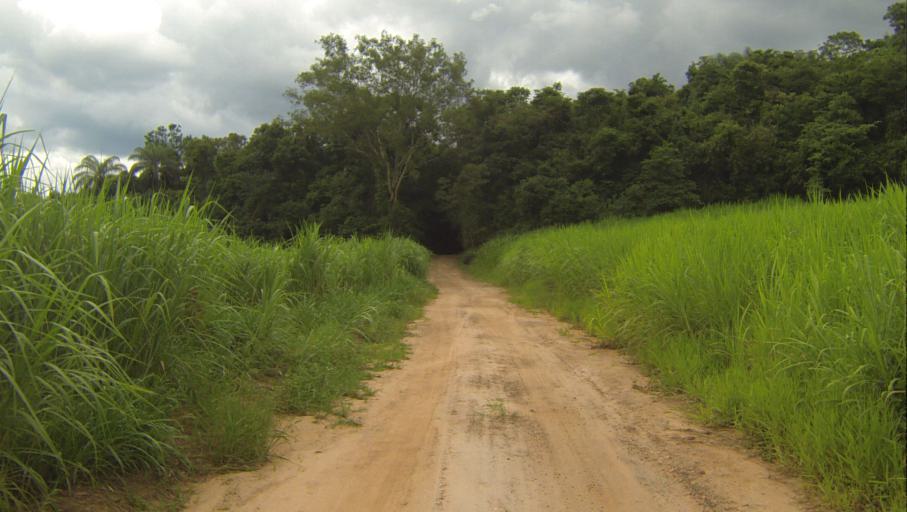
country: BR
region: Minas Gerais
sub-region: Brumadinho
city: Brumadinho
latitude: -20.1588
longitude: -44.1288
